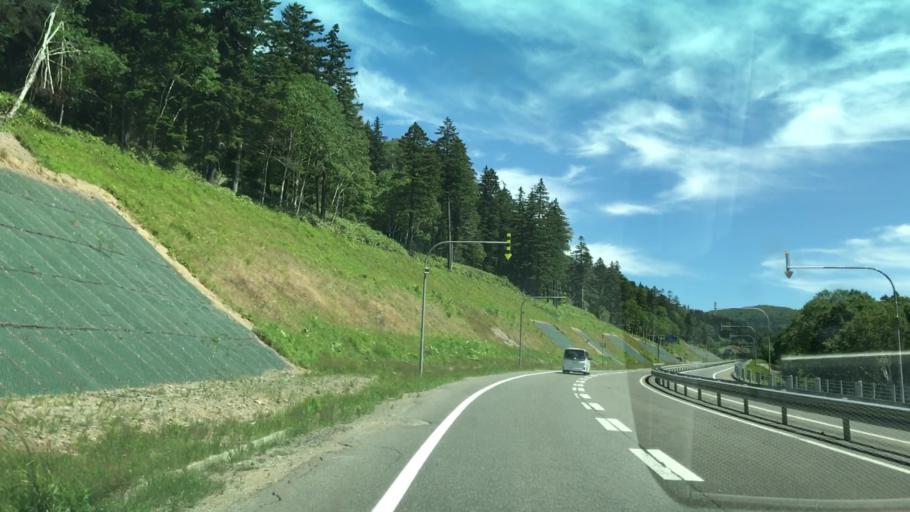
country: JP
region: Hokkaido
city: Otofuke
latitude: 42.9794
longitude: 142.7284
